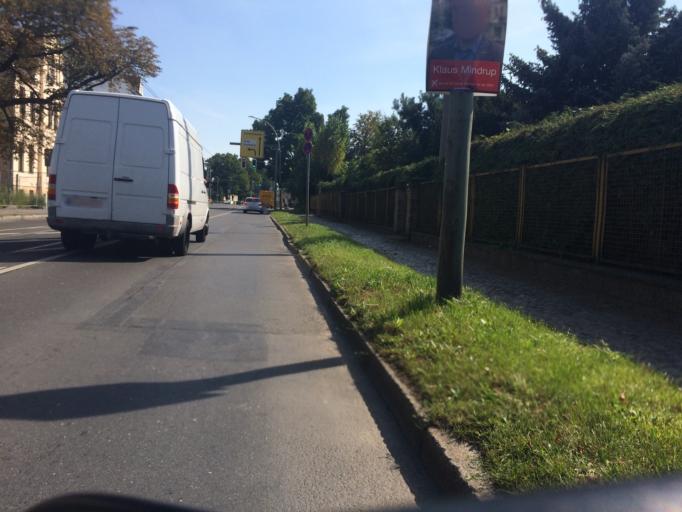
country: DE
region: Berlin
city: Heinersdorf
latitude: 52.5692
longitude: 13.4383
